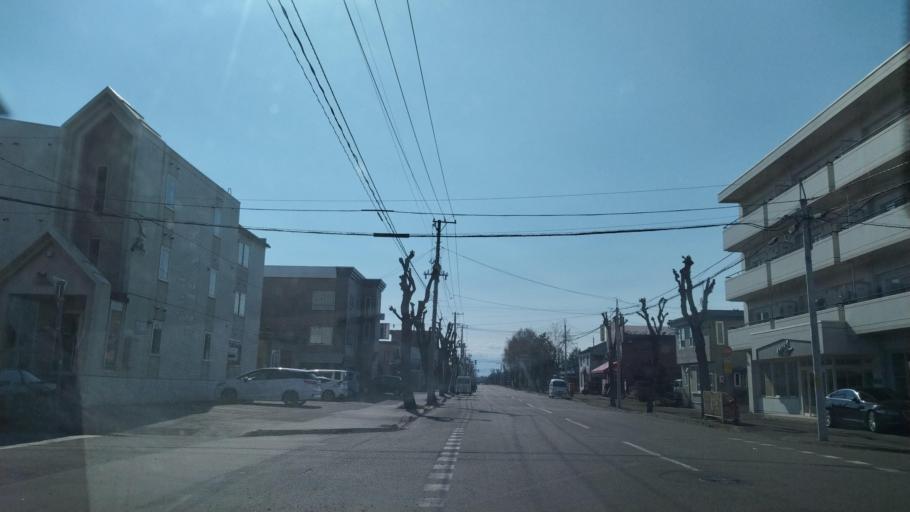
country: JP
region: Hokkaido
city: Obihiro
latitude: 42.9290
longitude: 143.1950
